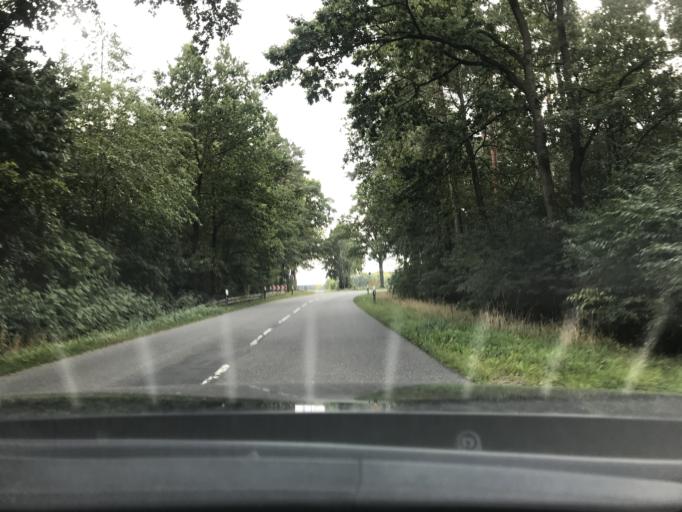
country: DE
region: Lower Saxony
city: Suderburg
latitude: 52.8847
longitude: 10.4425
